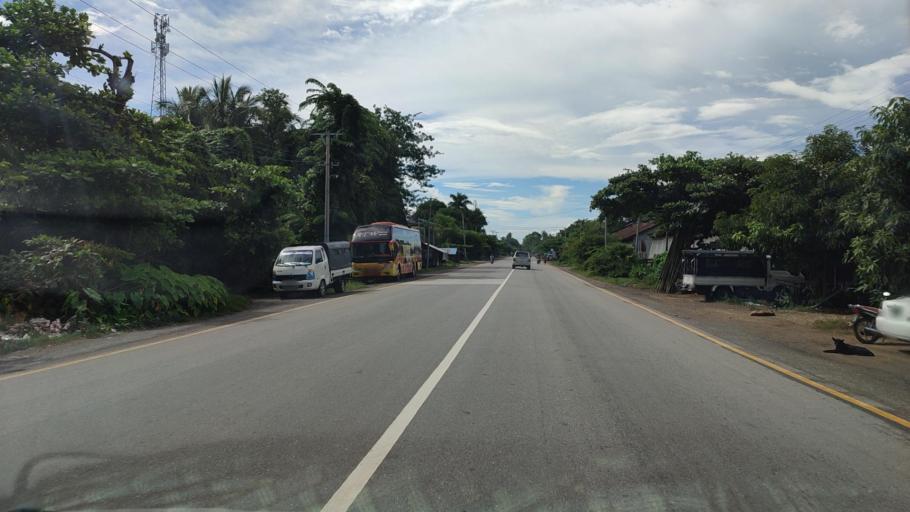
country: MM
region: Bago
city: Pyu
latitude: 18.3386
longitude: 96.4921
